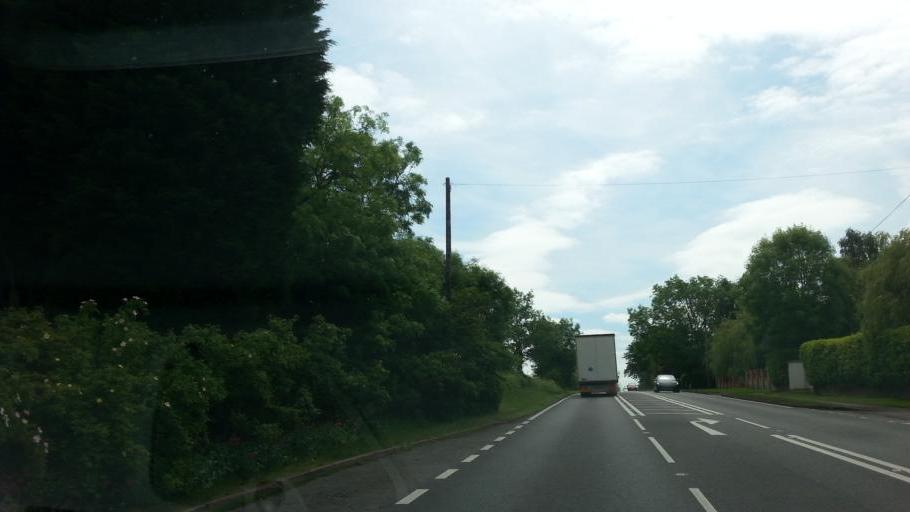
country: GB
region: England
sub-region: Nottinghamshire
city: Cotgrave
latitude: 52.8721
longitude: -1.0502
